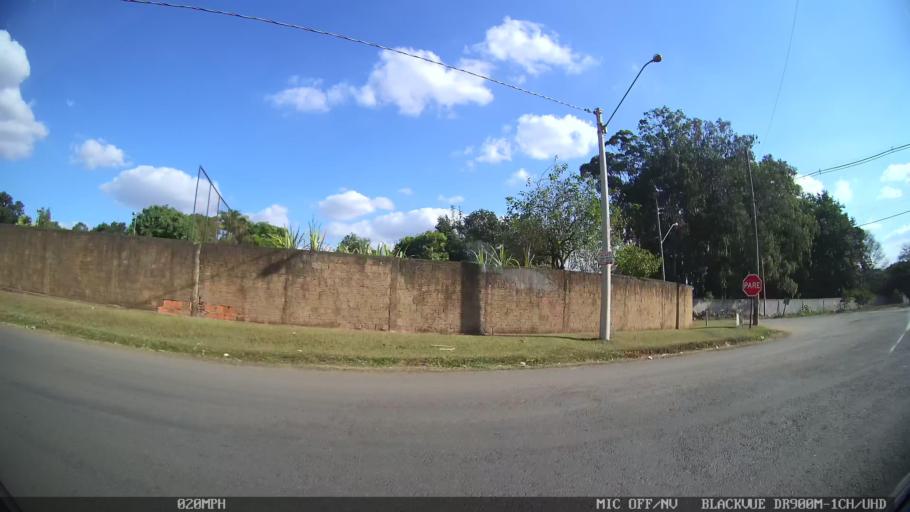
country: BR
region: Sao Paulo
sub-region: Nova Odessa
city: Nova Odessa
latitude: -22.8116
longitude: -47.3305
